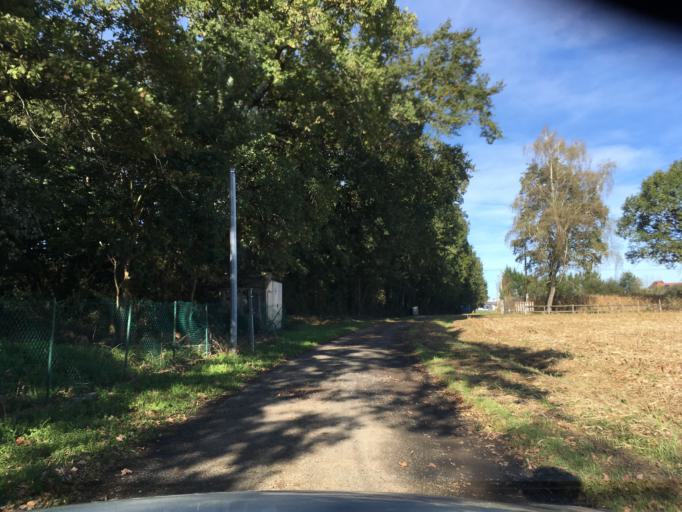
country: FR
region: Aquitaine
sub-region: Departement des Pyrenees-Atlantiques
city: Idron
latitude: 43.3130
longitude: -0.3114
